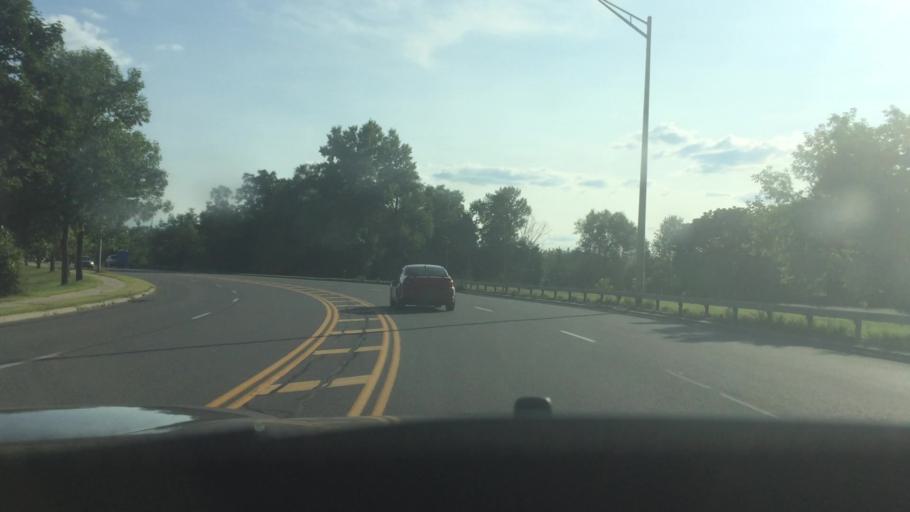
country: US
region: New York
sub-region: St. Lawrence County
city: Potsdam
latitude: 44.6721
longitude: -74.9900
